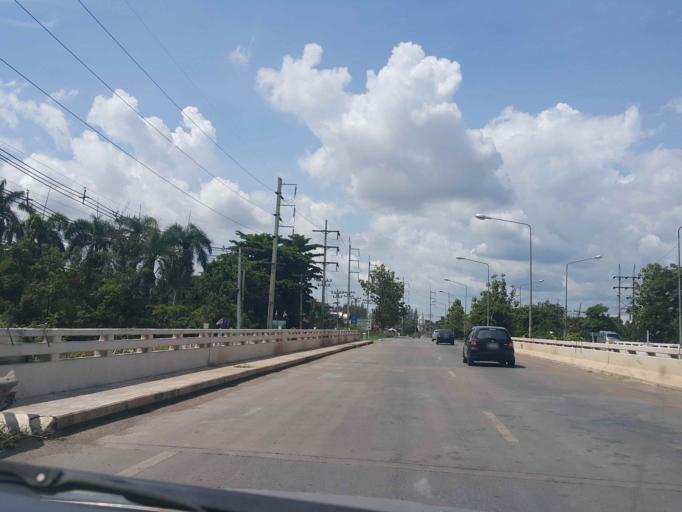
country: TH
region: Phayao
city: Phayao
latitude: 19.1602
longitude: 99.9144
